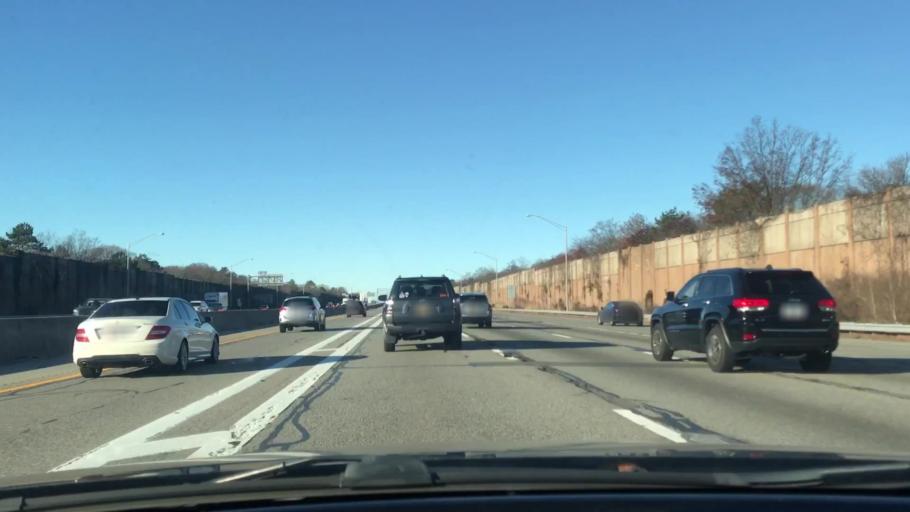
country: US
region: New York
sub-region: Suffolk County
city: Farmingville
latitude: 40.8232
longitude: -73.0272
